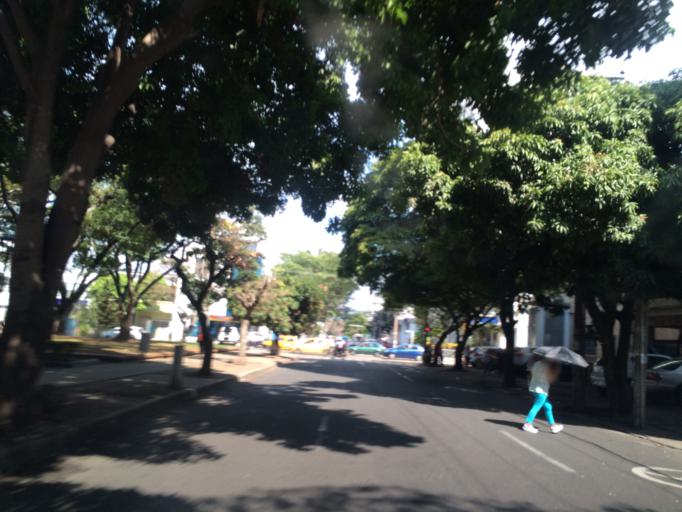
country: CO
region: Valle del Cauca
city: Cali
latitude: 3.4641
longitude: -76.5270
